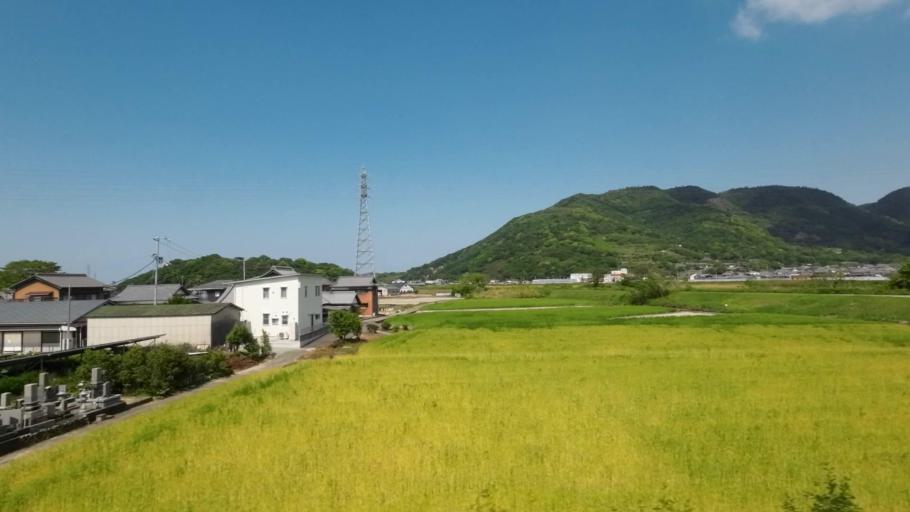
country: JP
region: Kagawa
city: Kan'onjicho
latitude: 34.1379
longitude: 133.6847
